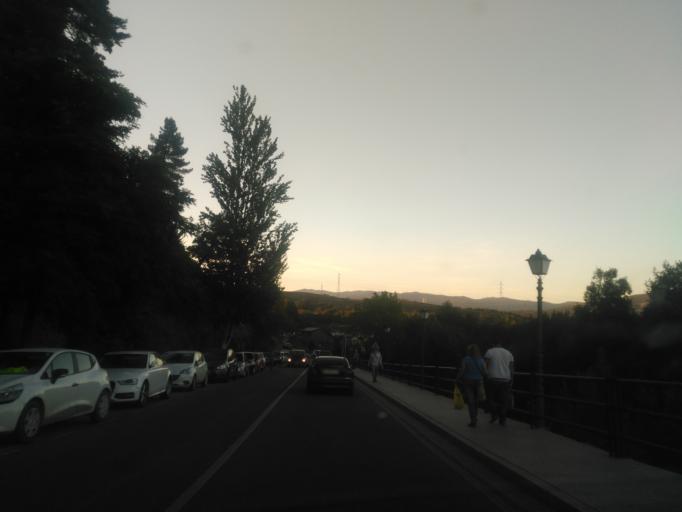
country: ES
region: Castille and Leon
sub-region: Provincia de Zamora
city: Puebla de Sanabria
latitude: 42.0543
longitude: -6.6328
